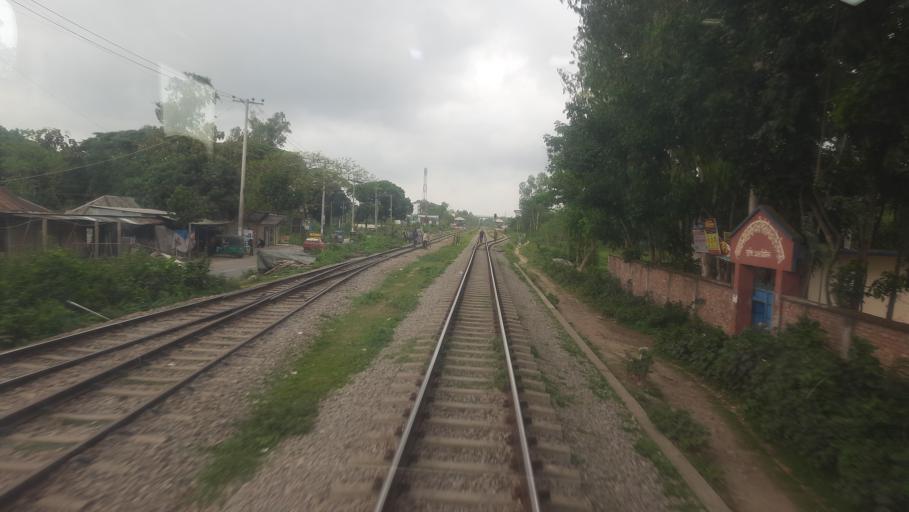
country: BD
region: Dhaka
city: Bhairab Bazar
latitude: 23.9943
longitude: 90.8709
